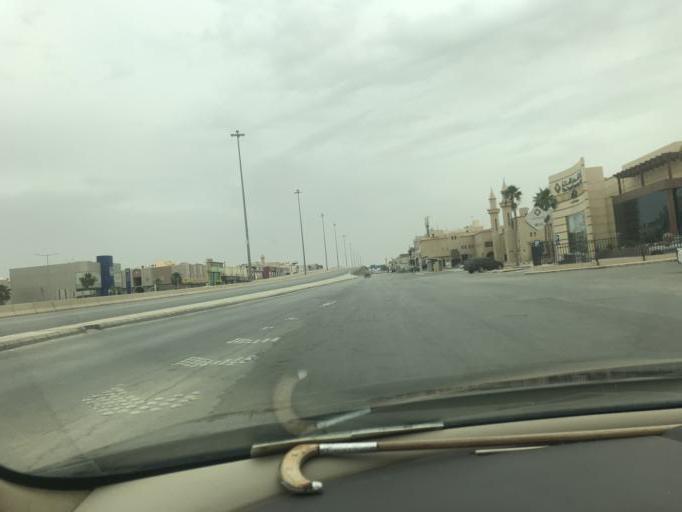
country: SA
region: Ar Riyad
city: Riyadh
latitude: 24.7949
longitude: 46.6991
